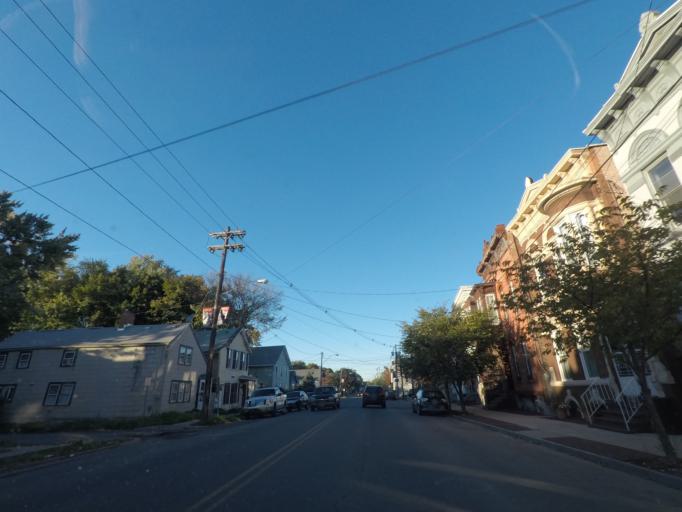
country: US
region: New York
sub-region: Albany County
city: Green Island
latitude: 42.7528
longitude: -73.6825
